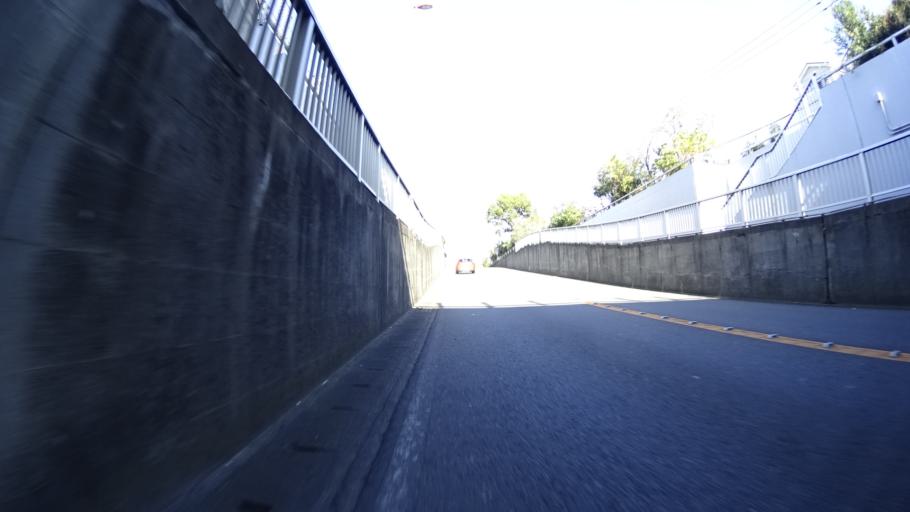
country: JP
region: Tokyo
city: Hachioji
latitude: 35.5850
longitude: 139.3636
